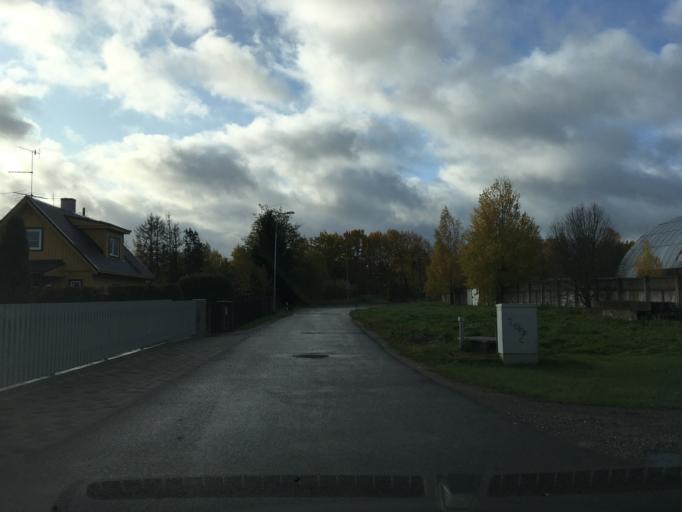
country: EE
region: Harju
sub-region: Keila linn
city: Keila
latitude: 59.3071
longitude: 24.4049
